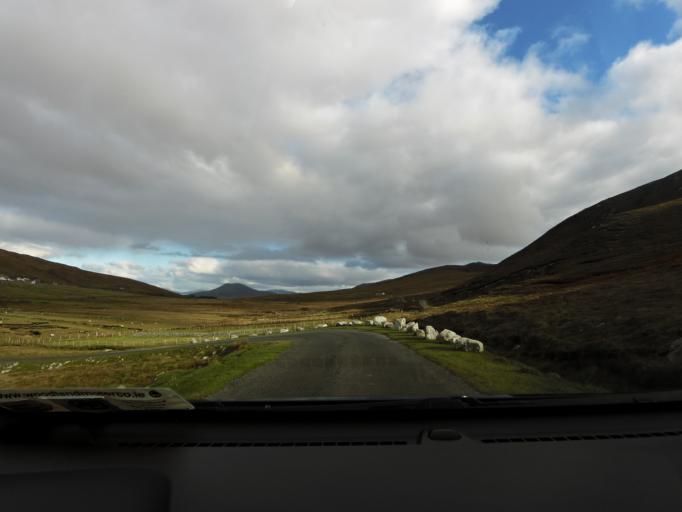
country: IE
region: Connaught
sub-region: Maigh Eo
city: Belmullet
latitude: 53.9004
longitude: -9.9930
